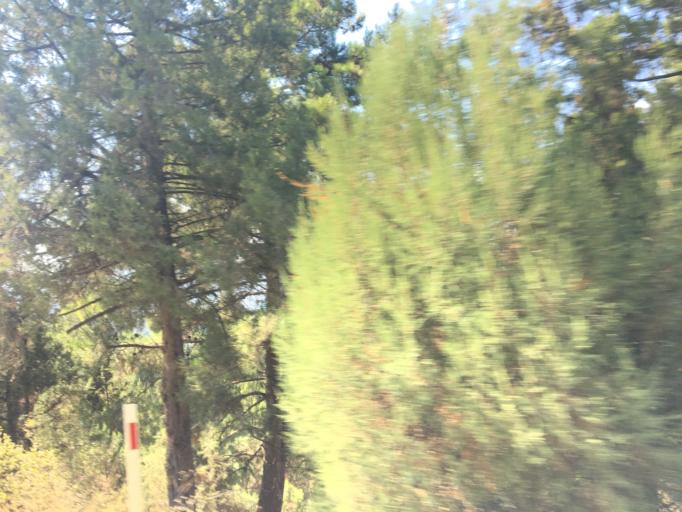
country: TR
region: Ankara
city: Beydili
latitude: 40.0642
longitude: 30.9220
